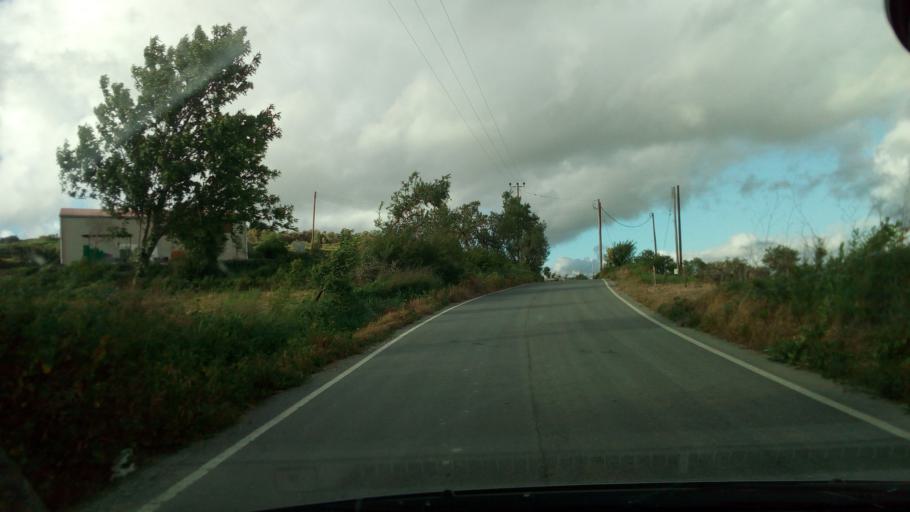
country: CY
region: Pafos
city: Mesogi
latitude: 34.8733
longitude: 32.5057
